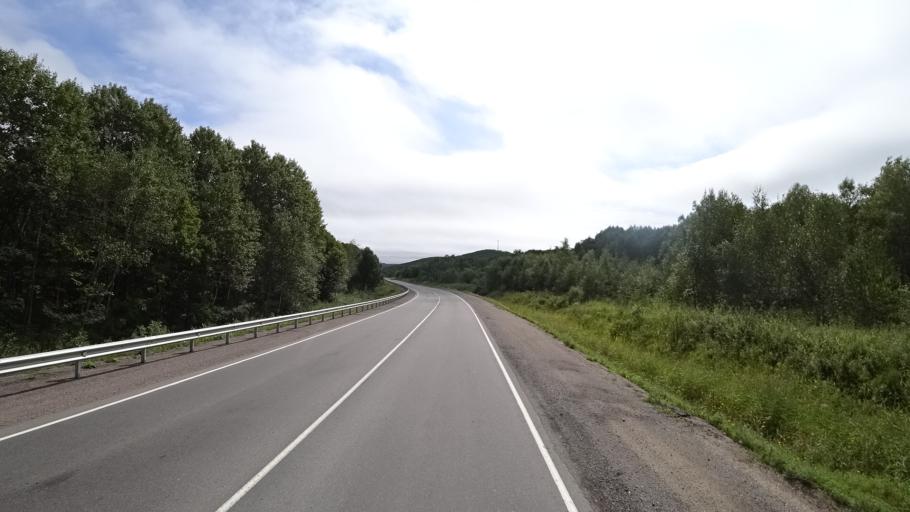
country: RU
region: Primorskiy
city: Lyalichi
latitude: 44.1174
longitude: 132.4192
